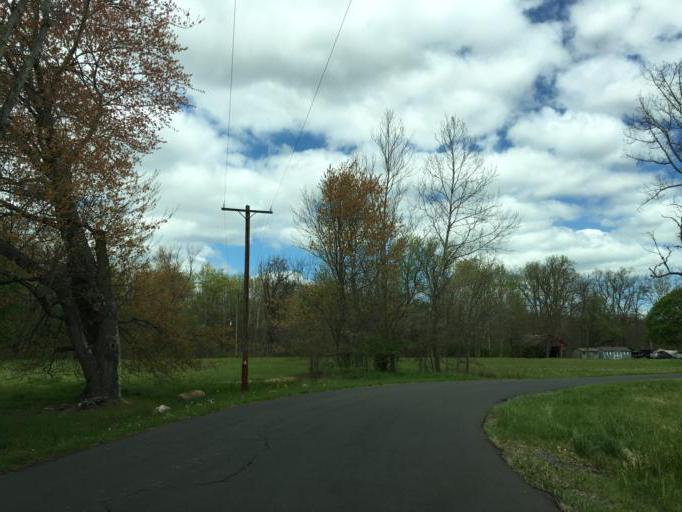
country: US
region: Maryland
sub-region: Frederick County
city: Thurmont
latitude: 39.6395
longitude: -77.3956
